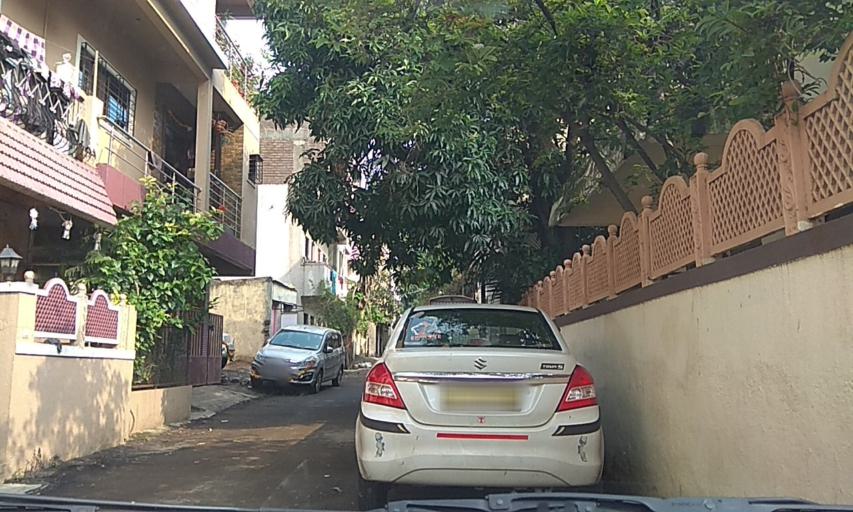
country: IN
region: Maharashtra
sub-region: Pune Division
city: Lohogaon
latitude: 18.5526
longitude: 73.9362
